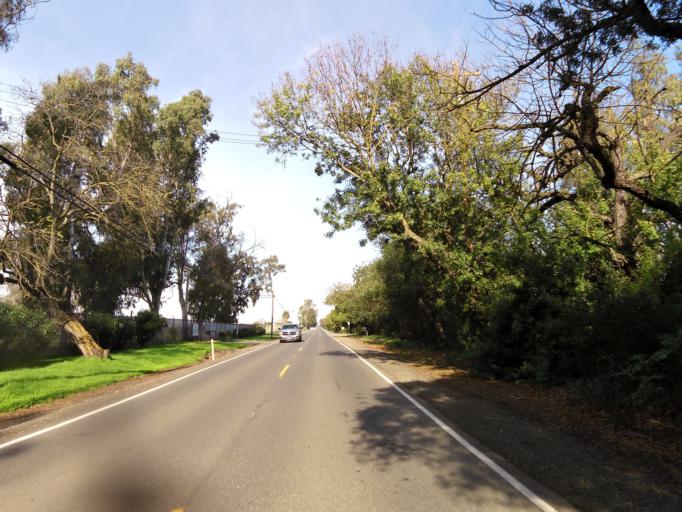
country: US
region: California
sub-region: San Joaquin County
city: Thornton
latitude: 38.3096
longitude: -121.4201
